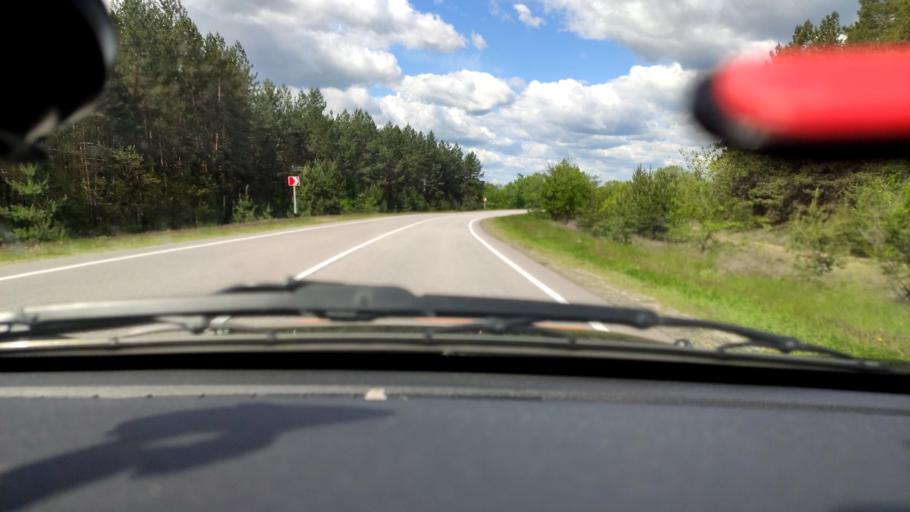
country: RU
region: Voronezj
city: Ostrogozhsk
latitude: 51.0526
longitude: 38.9382
